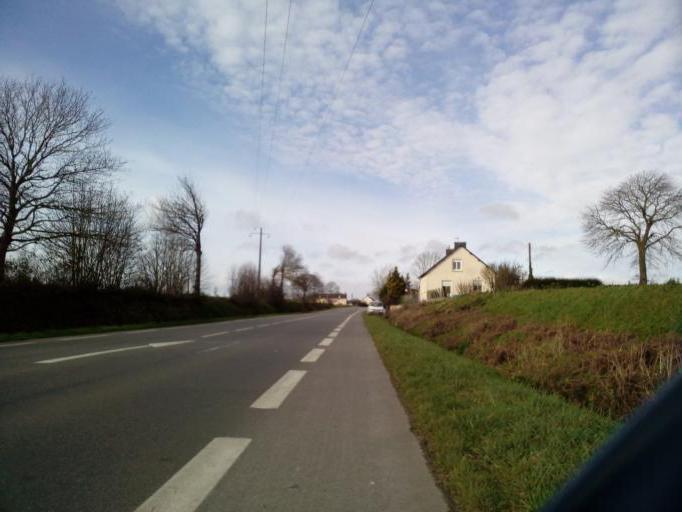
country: FR
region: Brittany
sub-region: Departement d'Ille-et-Vilaine
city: Montgermont
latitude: 48.1669
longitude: -1.7164
